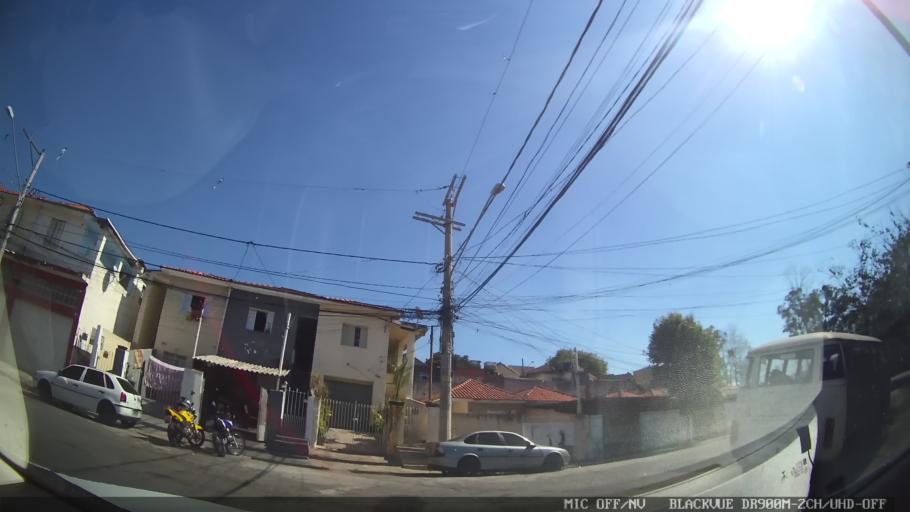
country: BR
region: Sao Paulo
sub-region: Sao Paulo
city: Sao Paulo
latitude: -23.4944
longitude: -46.6523
